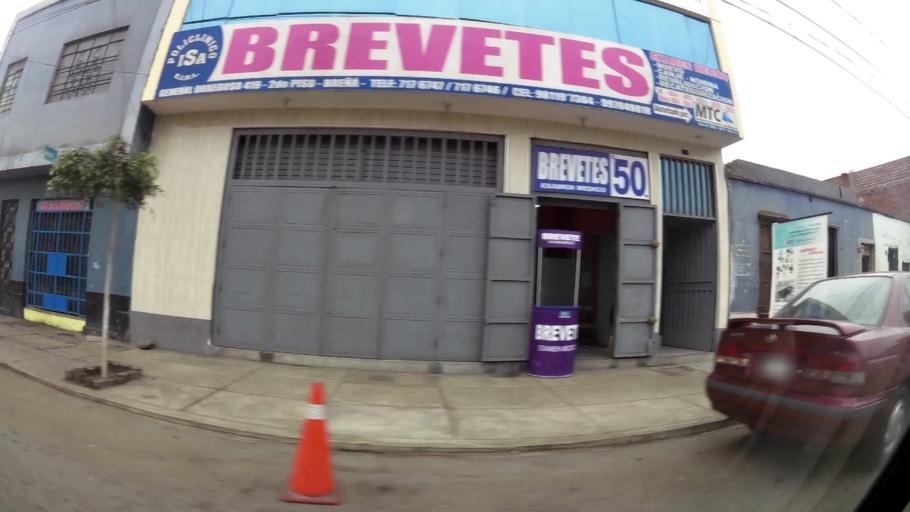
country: PE
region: Lima
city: Lima
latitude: -12.0654
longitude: -77.0517
